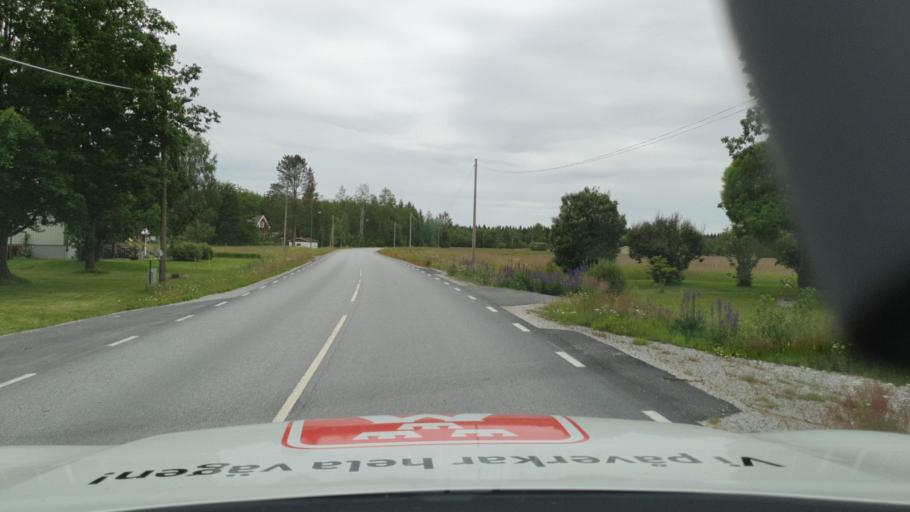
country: SE
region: Vaesterbotten
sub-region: Nordmalings Kommun
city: Nordmaling
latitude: 63.5618
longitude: 19.4112
